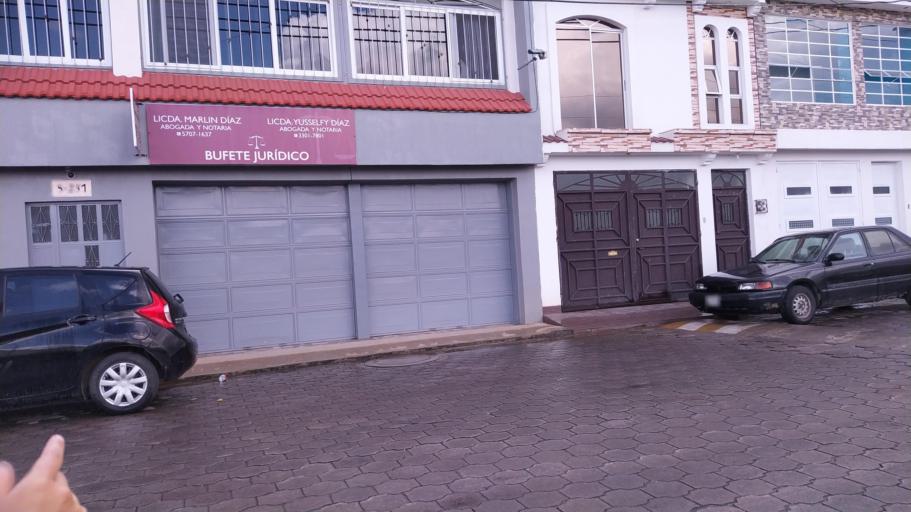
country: GT
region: Quetzaltenango
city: Quetzaltenango
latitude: 14.8548
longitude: -91.5099
